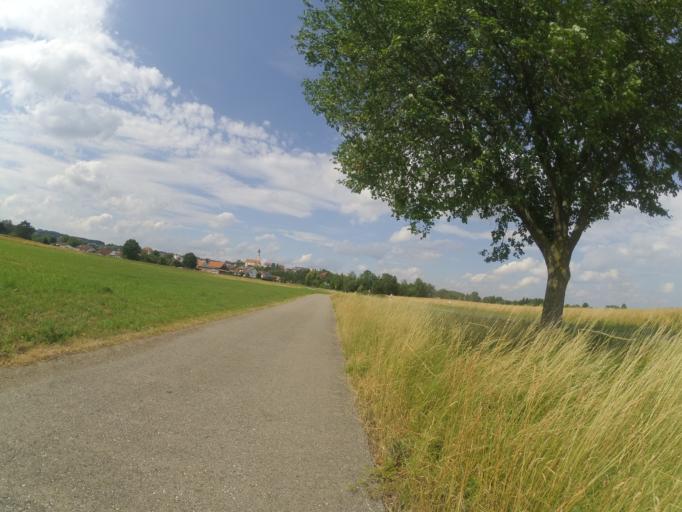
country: DE
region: Baden-Wuerttemberg
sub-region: Tuebingen Region
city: Opfingen
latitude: 48.2797
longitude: 9.8037
